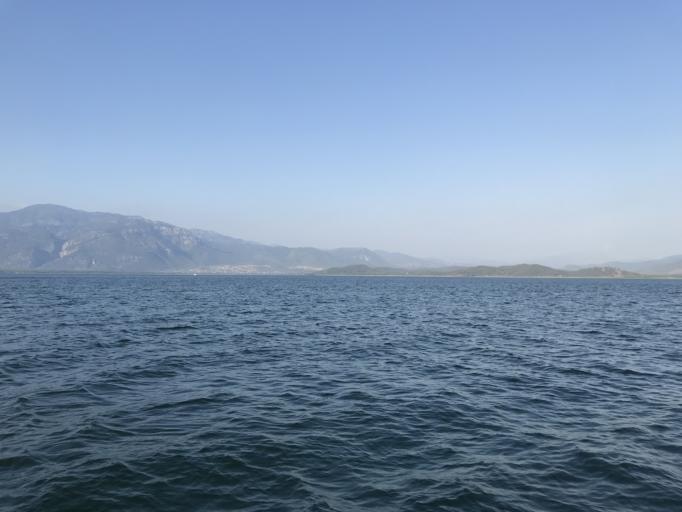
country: TR
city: Dalyan
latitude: 36.9185
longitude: 28.6491
